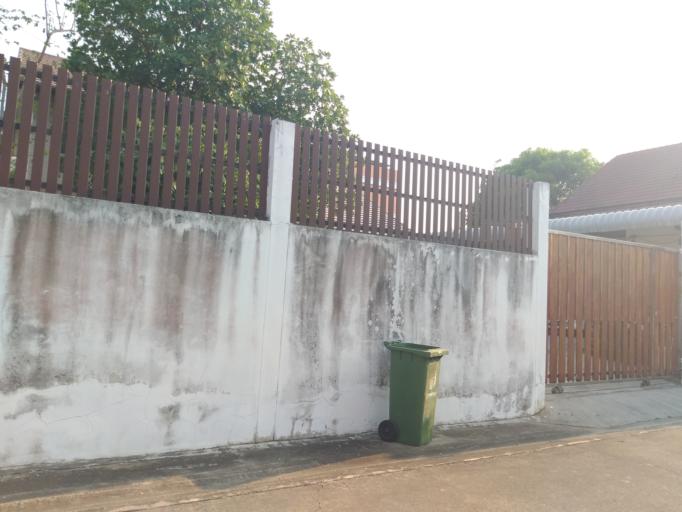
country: TH
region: Bangkok
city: Lat Phrao
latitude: 13.8218
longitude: 100.6125
